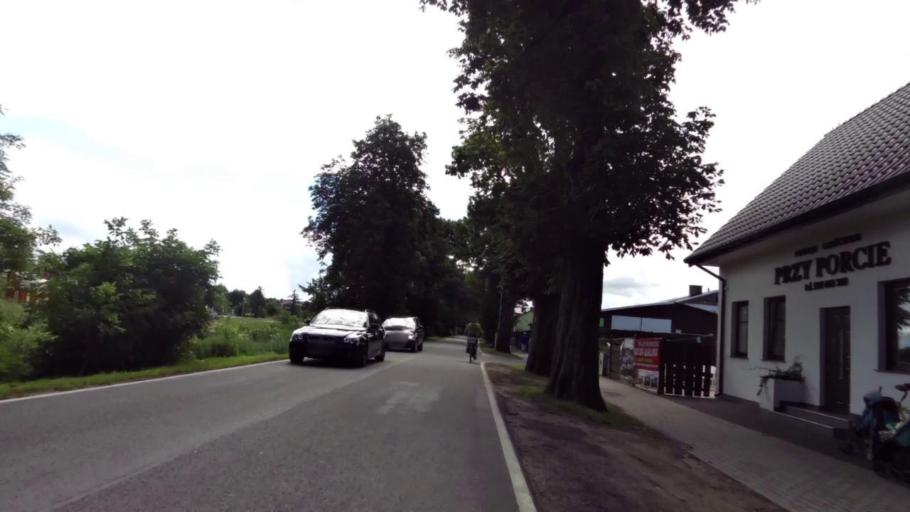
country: PL
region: West Pomeranian Voivodeship
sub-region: Powiat slawienski
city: Darlowo
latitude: 54.4388
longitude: 16.3854
